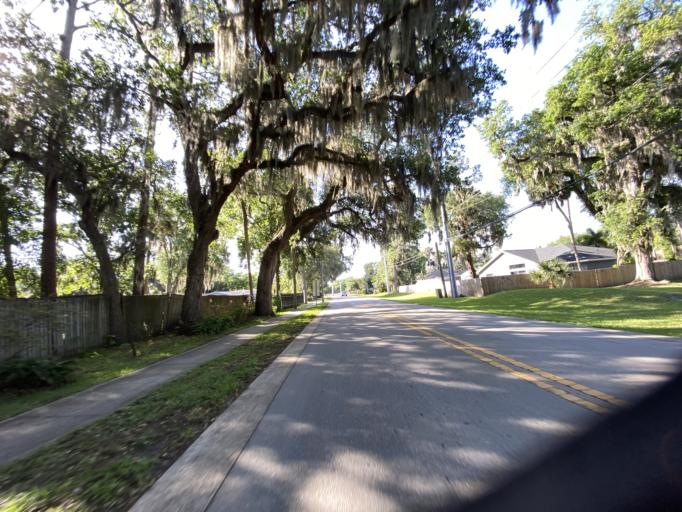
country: US
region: Florida
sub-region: Volusia County
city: South Daytona
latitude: 29.1746
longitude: -81.0218
